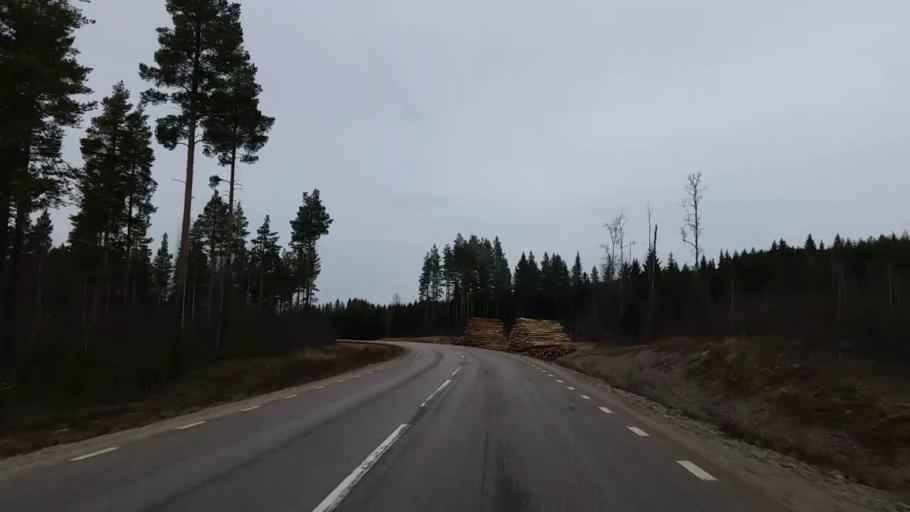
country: SE
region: Gaevleborg
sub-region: Ovanakers Kommun
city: Edsbyn
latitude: 61.1737
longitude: 15.8843
